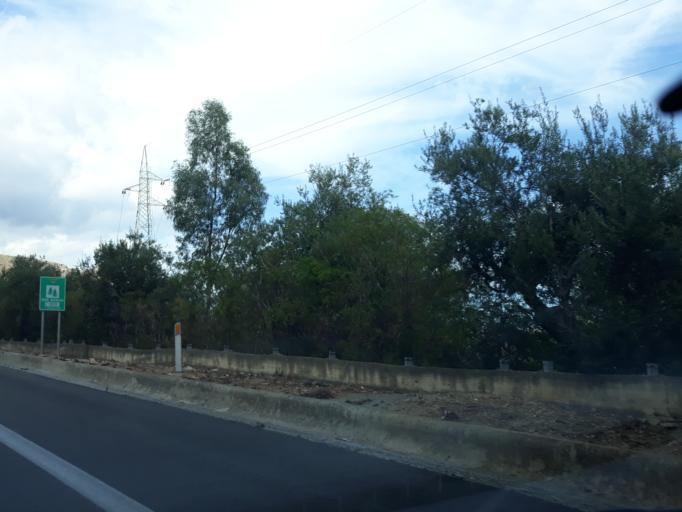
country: IT
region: Sicily
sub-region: Palermo
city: Termini Imerese
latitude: 37.9823
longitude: 13.6658
